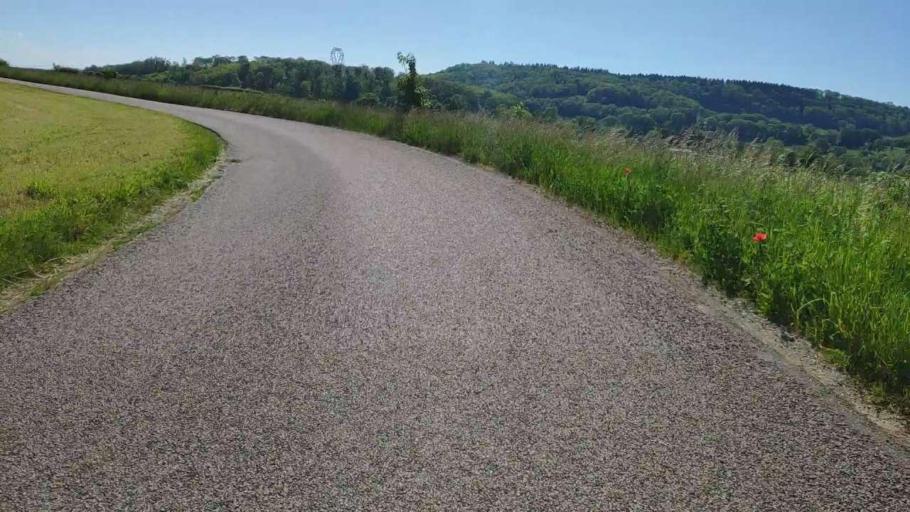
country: FR
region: Franche-Comte
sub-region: Departement du Jura
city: Perrigny
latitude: 46.7173
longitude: 5.5690
